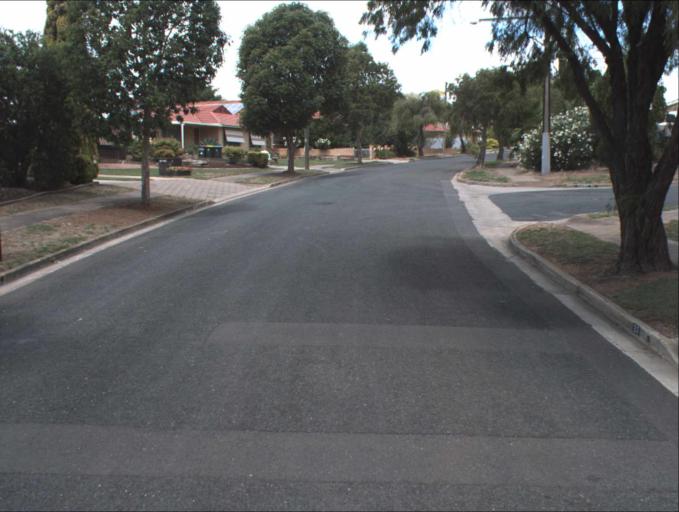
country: AU
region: South Australia
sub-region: Port Adelaide Enfield
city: Gilles Plains
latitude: -34.8407
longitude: 138.6535
